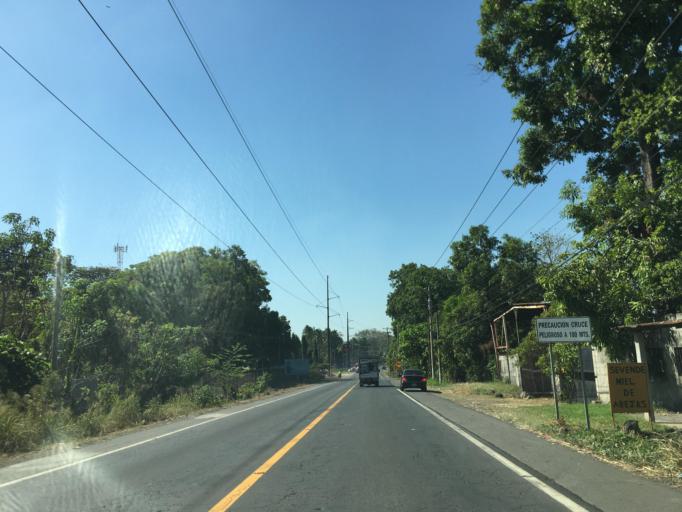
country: GT
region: Escuintla
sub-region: Municipio de Escuintla
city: Escuintla
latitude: 14.2720
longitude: -90.7920
